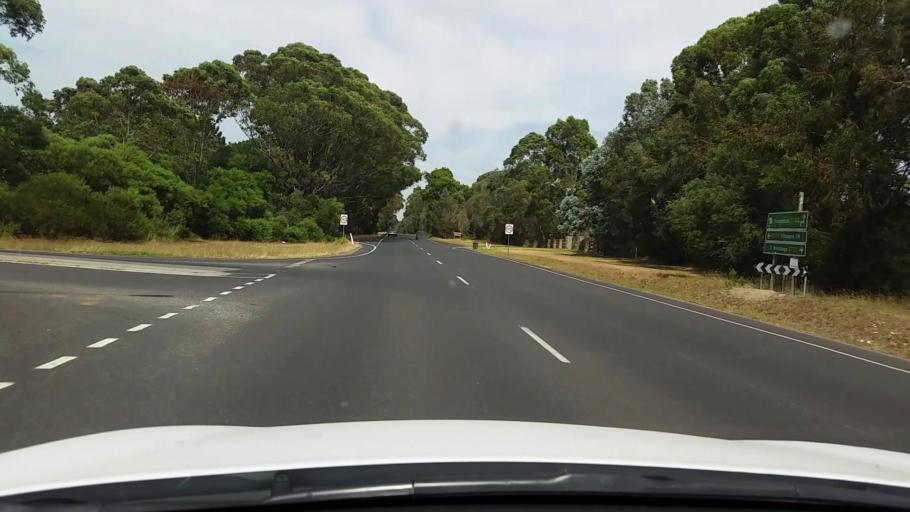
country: AU
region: Victoria
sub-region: Mornington Peninsula
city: Balnarring
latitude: -38.3609
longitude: 145.1450
